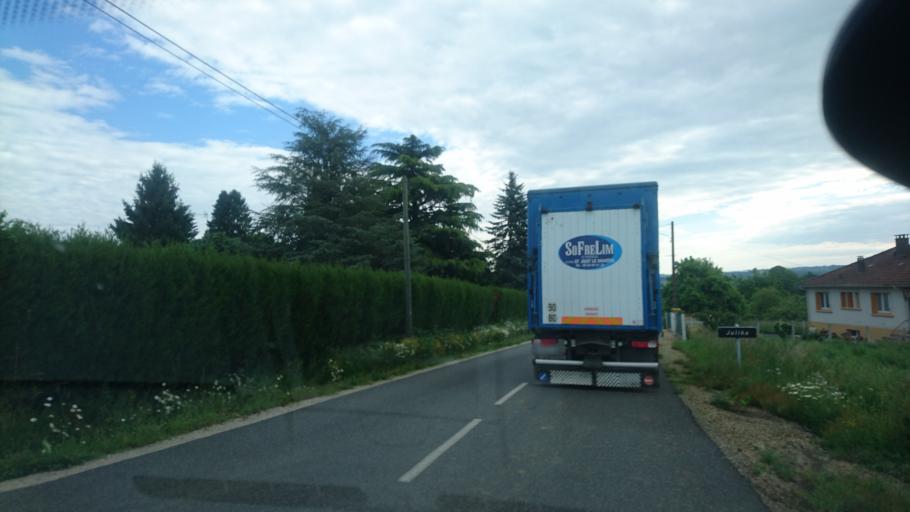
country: FR
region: Limousin
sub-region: Departement de la Haute-Vienne
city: Chateauneuf-la-Foret
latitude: 45.7046
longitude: 1.5865
